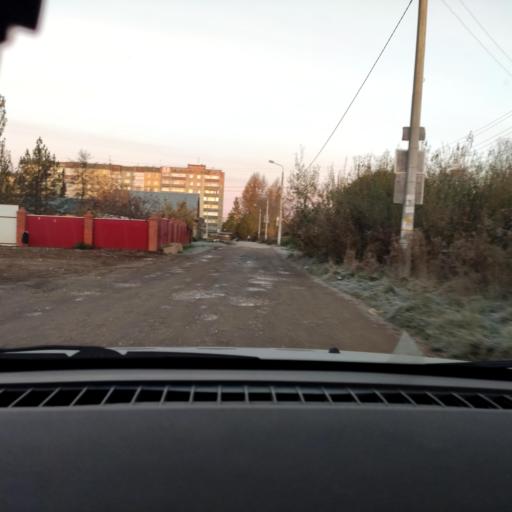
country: RU
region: Perm
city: Perm
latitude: 58.0554
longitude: 56.3588
